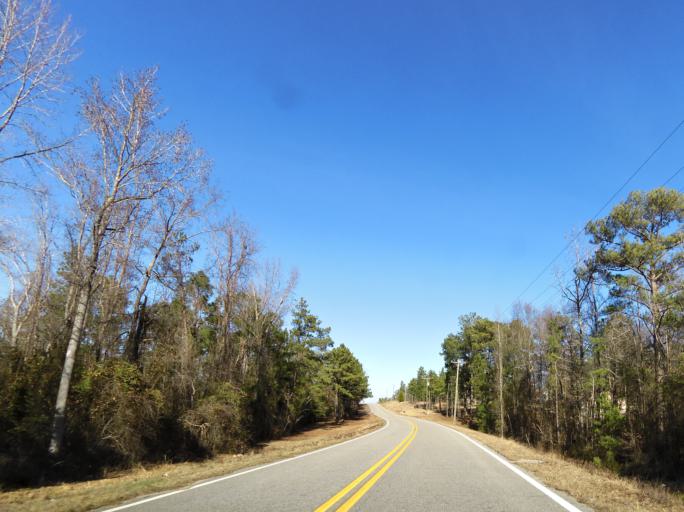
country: US
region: Georgia
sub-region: Crawford County
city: Knoxville
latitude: 32.7441
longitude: -83.9033
